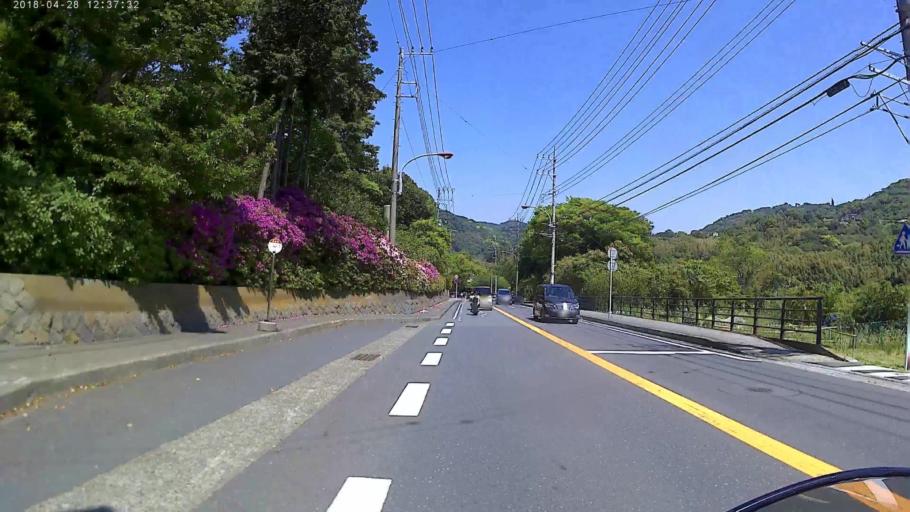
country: JP
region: Kanagawa
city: Hayama
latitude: 35.2654
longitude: 139.6004
